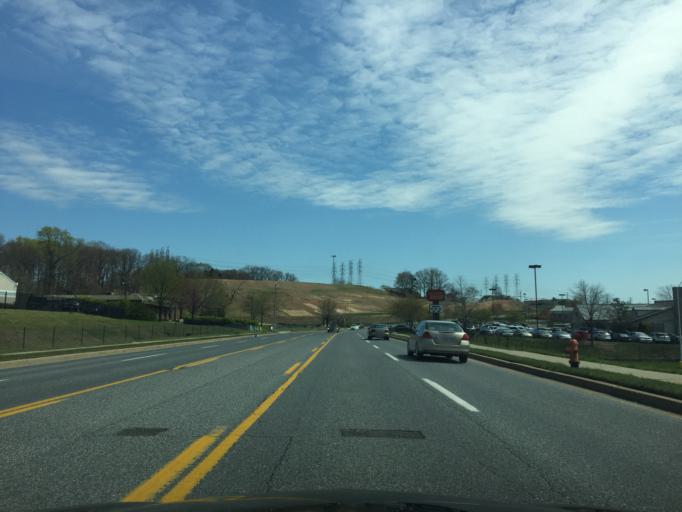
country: US
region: Maryland
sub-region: Baltimore County
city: Overlea
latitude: 39.3730
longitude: -76.5066
